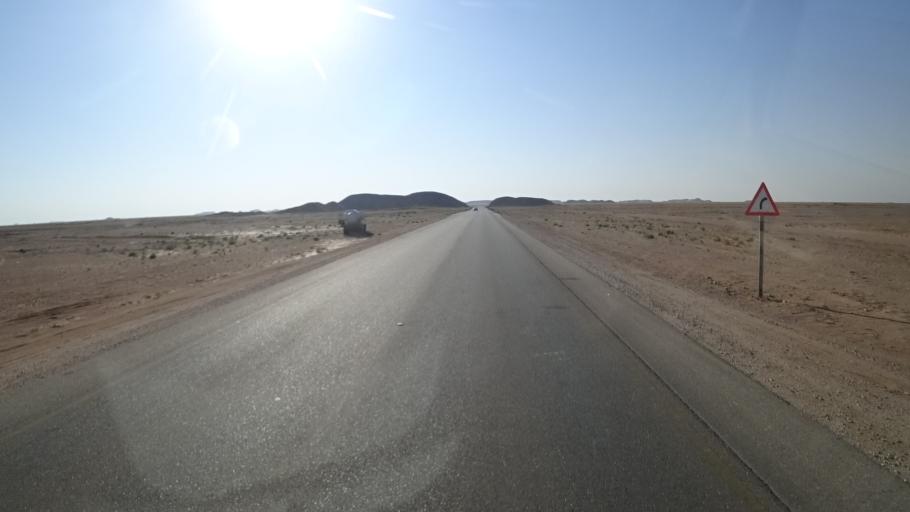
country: OM
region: Zufar
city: Salalah
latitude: 17.6396
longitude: 53.8952
